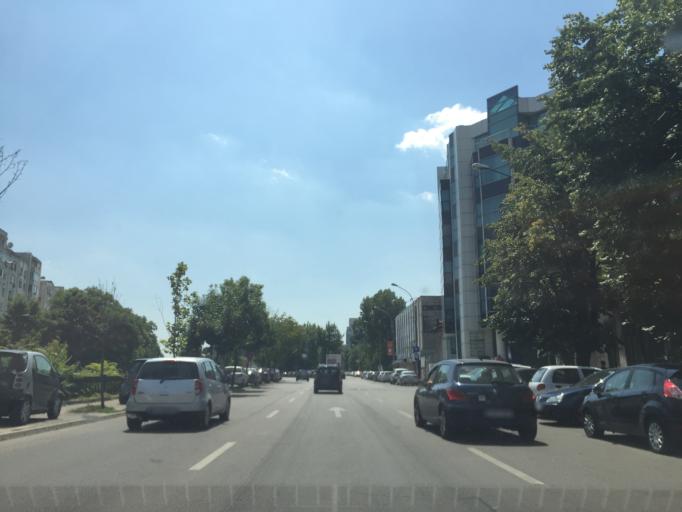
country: RO
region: Bucuresti
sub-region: Municipiul Bucuresti
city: Bucharest
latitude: 44.4202
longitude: 26.1105
